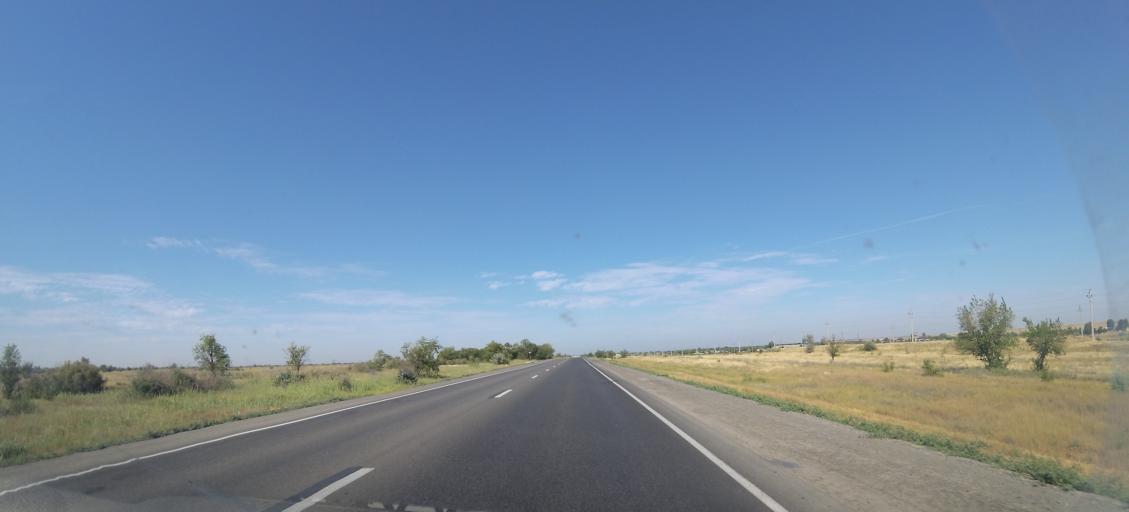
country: RU
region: Volgograd
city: Bereslavka
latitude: 48.6844
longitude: 43.9323
